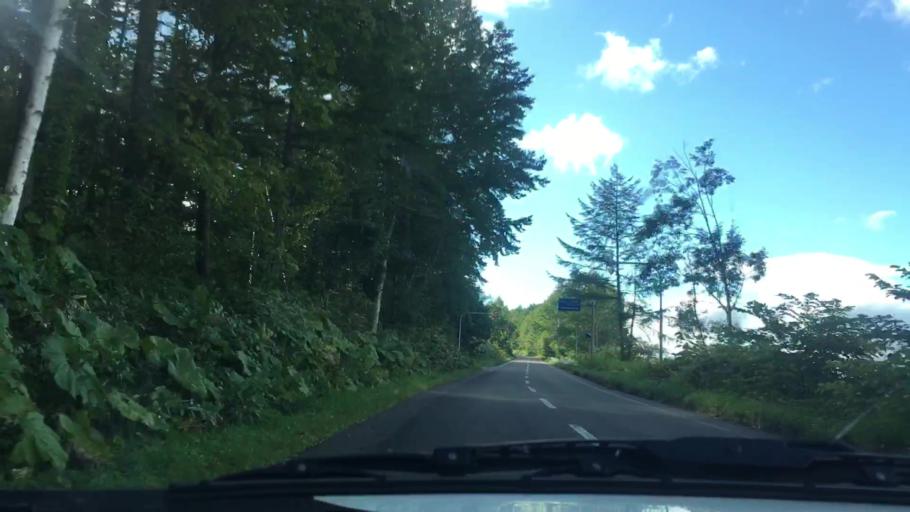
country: JP
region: Hokkaido
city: Otofuke
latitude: 43.1711
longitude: 142.9762
